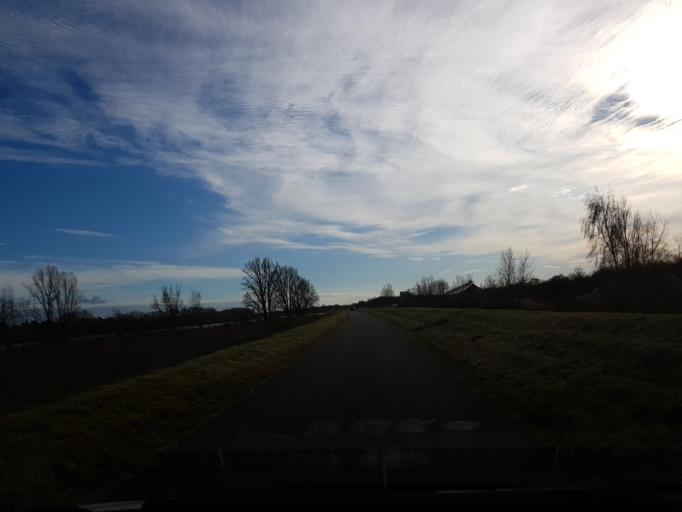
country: FR
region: Centre
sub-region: Departement du Loiret
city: Sandillon
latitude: 47.8690
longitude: 2.0265
